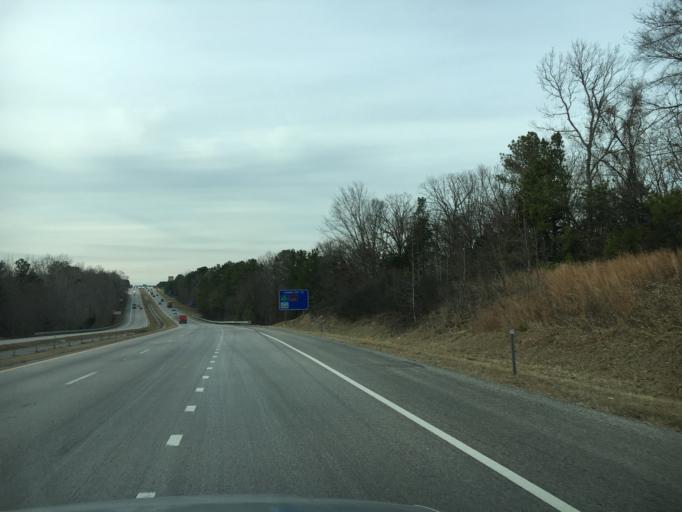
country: US
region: South Carolina
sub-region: Laurens County
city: Clinton
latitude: 34.4989
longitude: -81.8465
